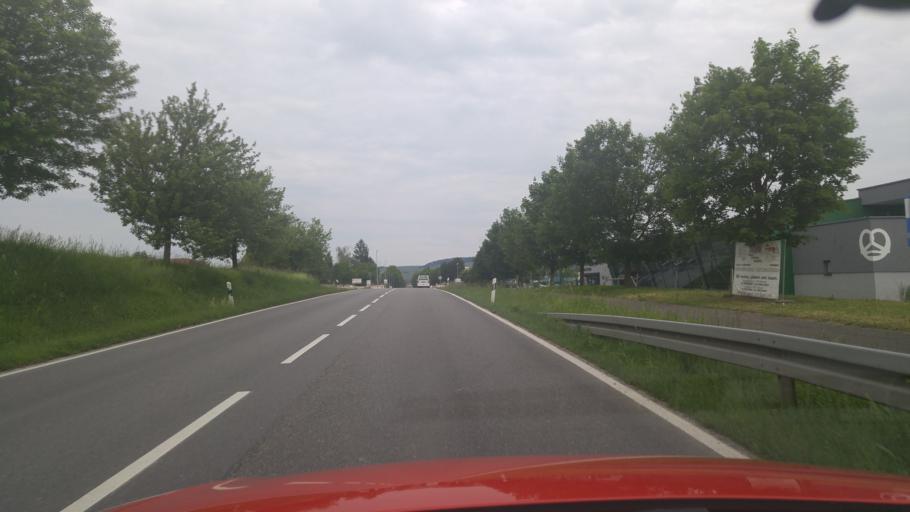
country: DE
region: Baden-Wuerttemberg
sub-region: Regierungsbezirk Stuttgart
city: Lehrensteinsfeld
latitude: 49.1264
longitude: 9.3632
